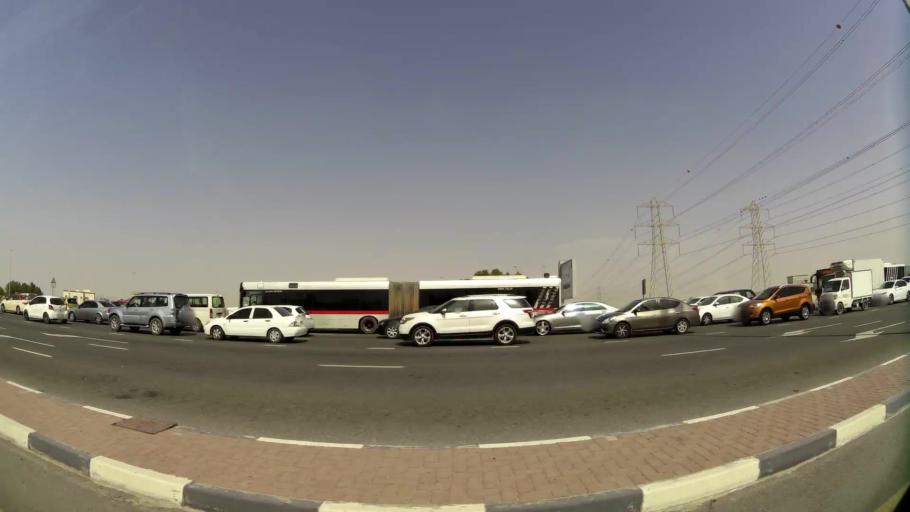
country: AE
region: Ash Shariqah
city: Sharjah
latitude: 25.2698
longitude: 55.3954
